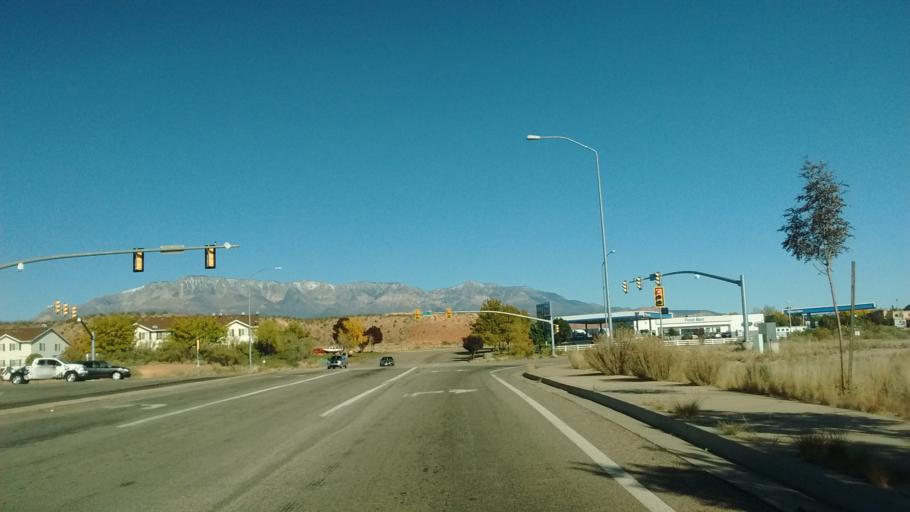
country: US
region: Utah
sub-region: Washington County
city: Washington
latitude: 37.1598
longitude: -113.4355
